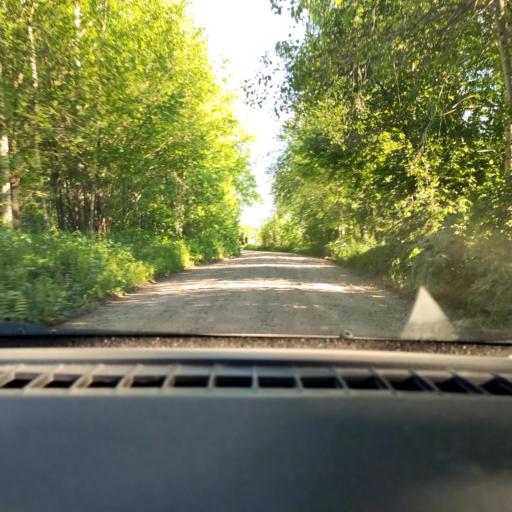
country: RU
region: Perm
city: Overyata
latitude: 58.1221
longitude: 55.8811
